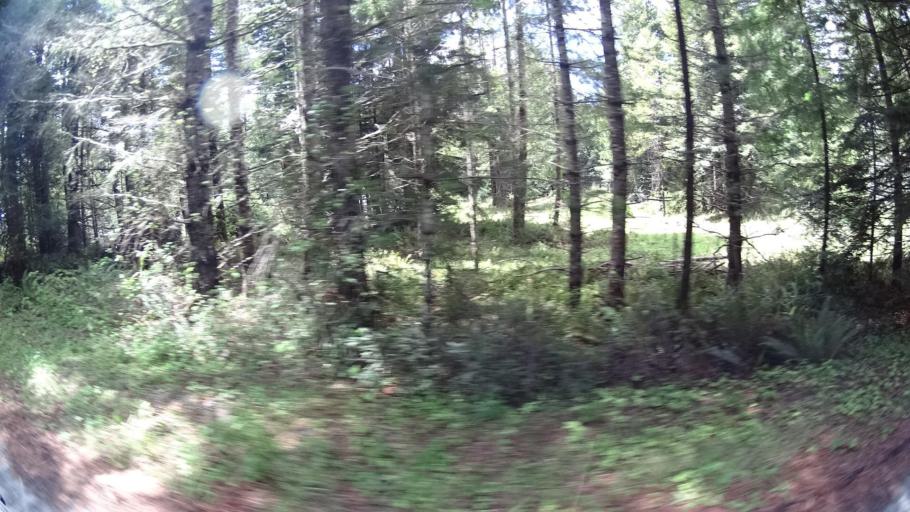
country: US
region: California
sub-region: Humboldt County
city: Blue Lake
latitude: 40.8457
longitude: -123.9242
